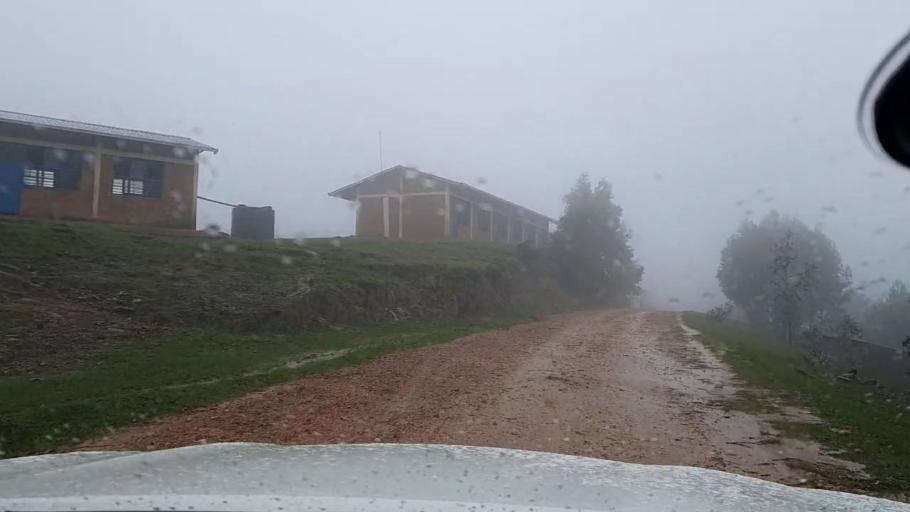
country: RW
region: Western Province
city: Kibuye
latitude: -2.1370
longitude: 29.4677
